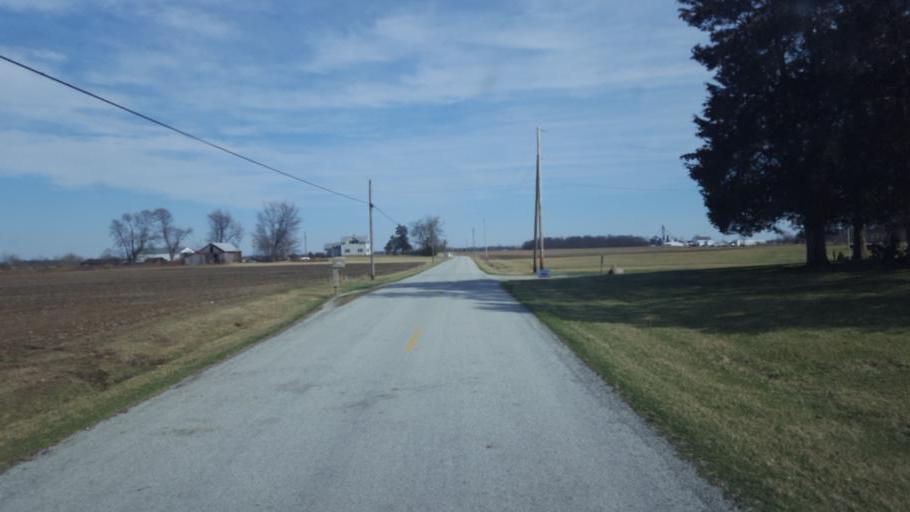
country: US
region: Ohio
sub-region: Hardin County
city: Kenton
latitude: 40.6575
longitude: -83.4886
